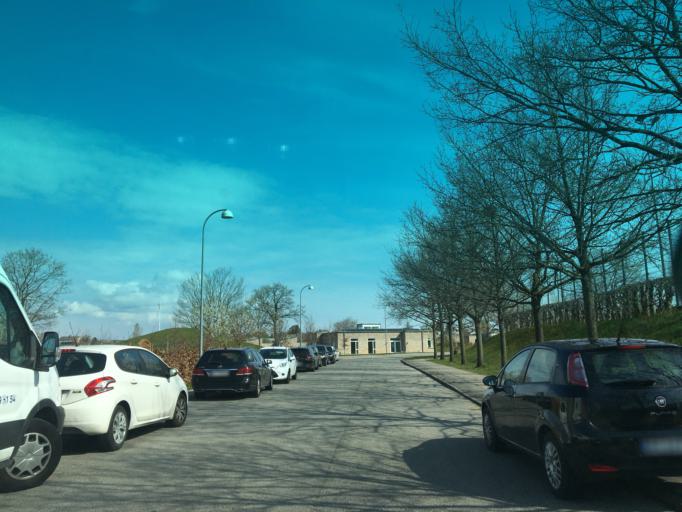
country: DK
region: Capital Region
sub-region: Gladsaxe Municipality
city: Buddinge
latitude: 55.7453
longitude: 12.4676
